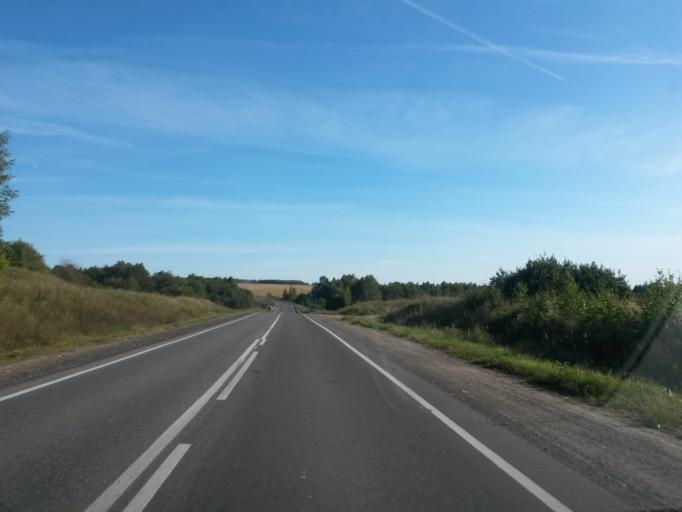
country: RU
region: Jaroslavl
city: Gavrilov-Yam
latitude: 57.3312
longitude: 39.9211
